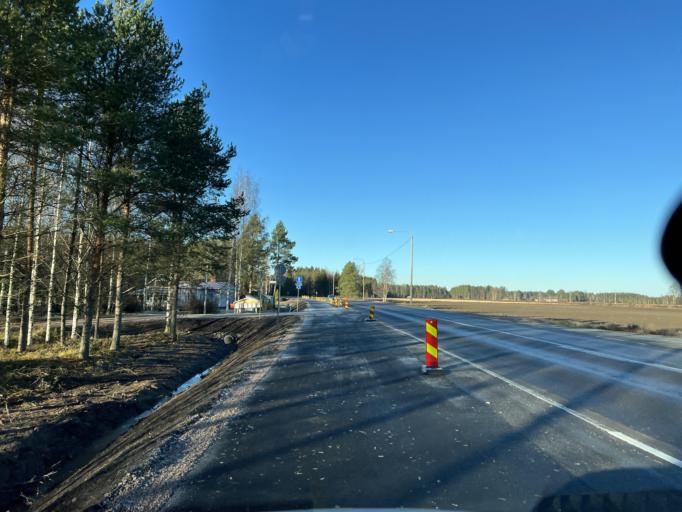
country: FI
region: Northern Ostrobothnia
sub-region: Nivala-Haapajaervi
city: Nivala
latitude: 63.9489
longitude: 24.9226
